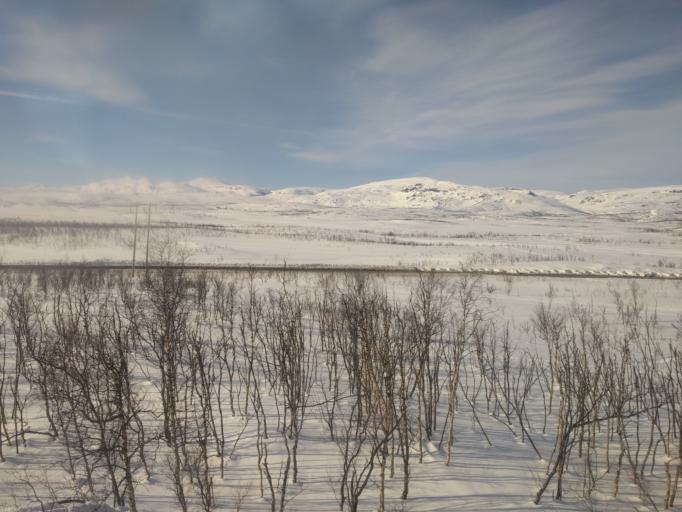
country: NO
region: Troms
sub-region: Bardu
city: Setermoen
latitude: 68.4273
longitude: 18.3967
